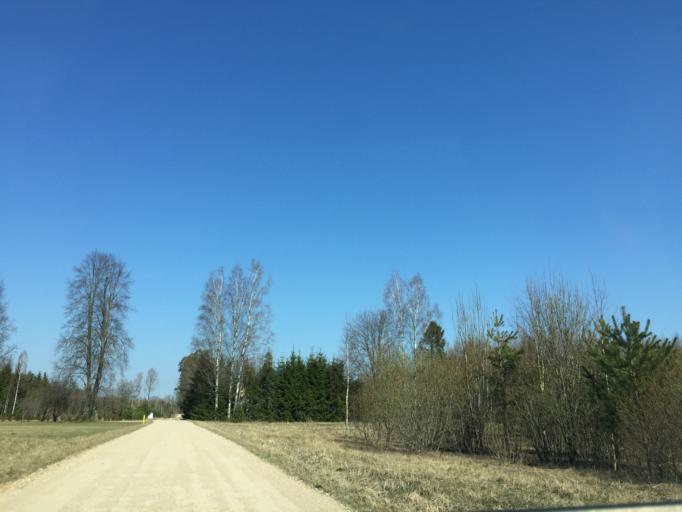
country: EE
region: Tartu
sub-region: Alatskivi vald
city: Kallaste
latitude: 58.5368
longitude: 26.9456
